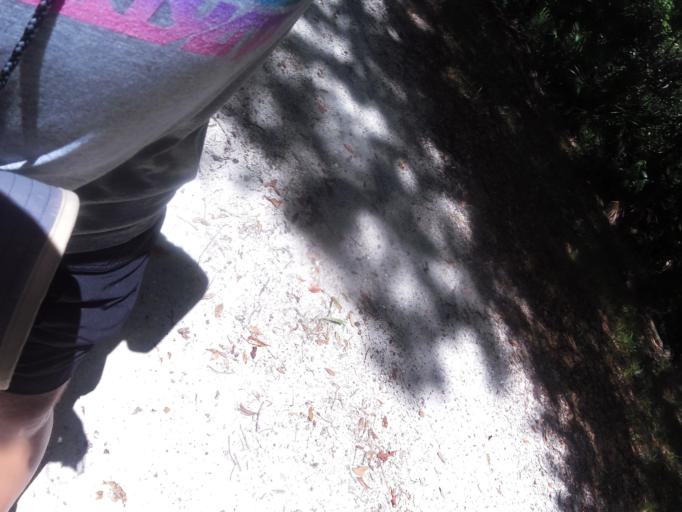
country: US
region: Florida
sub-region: Saint Johns County
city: Villano Beach
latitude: 30.0427
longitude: -81.3378
